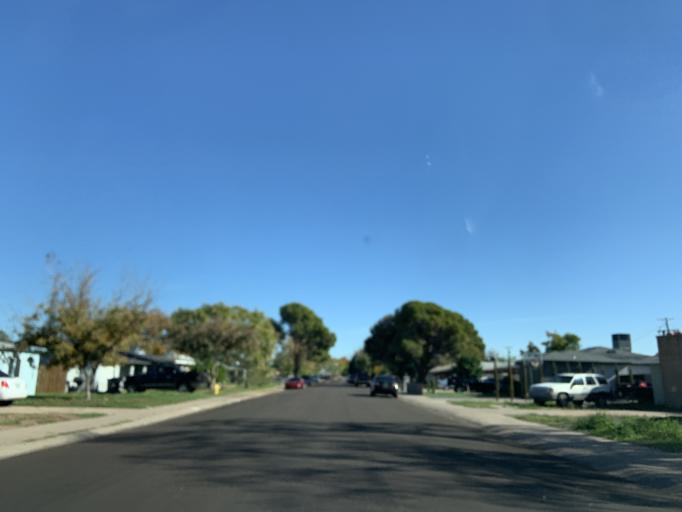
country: US
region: Arizona
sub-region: Maricopa County
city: Mesa
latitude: 33.4181
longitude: -111.8593
